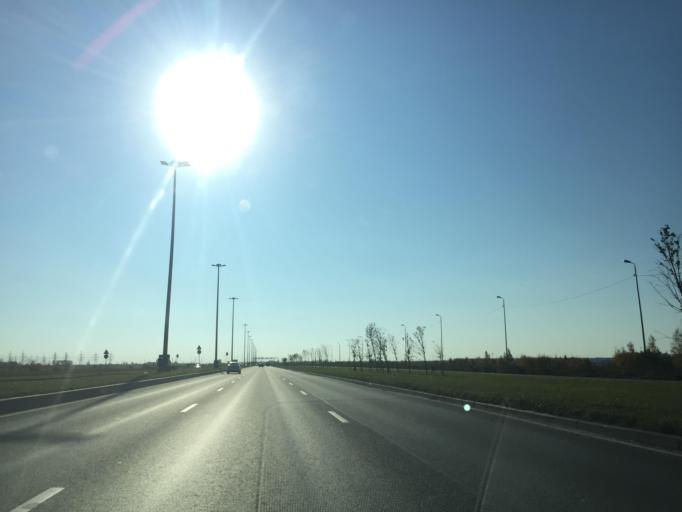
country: RU
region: St.-Petersburg
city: Petro-Slavyanka
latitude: 59.7771
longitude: 30.4983
